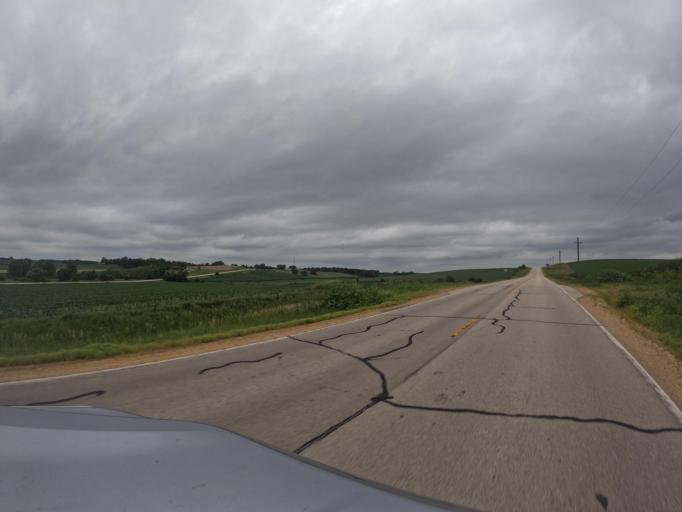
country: US
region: Iowa
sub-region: Clinton County
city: De Witt
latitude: 41.9331
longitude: -90.6065
